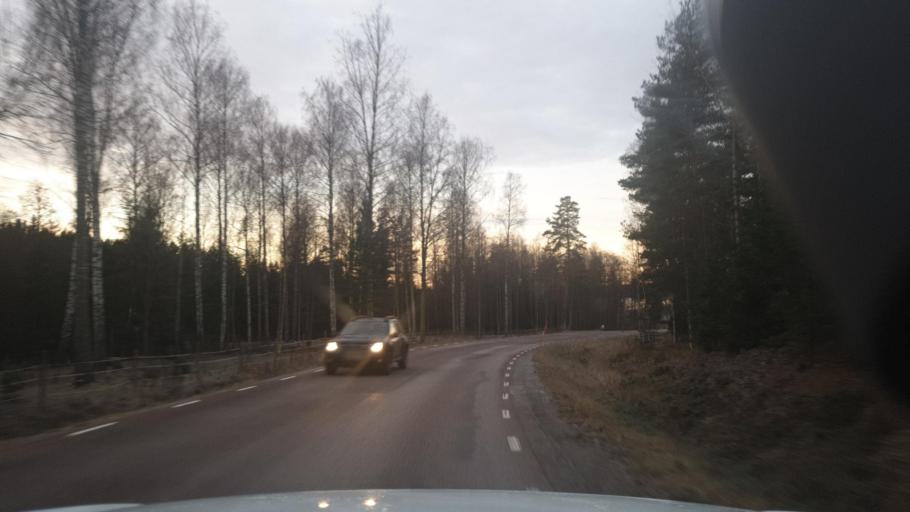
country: SE
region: Vaermland
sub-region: Arvika Kommun
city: Arvika
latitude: 59.5782
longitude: 12.7213
